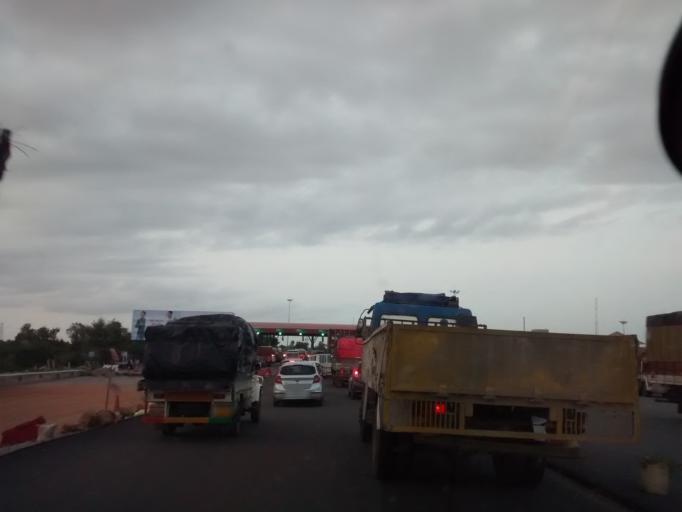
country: IN
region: Telangana
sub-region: Mahbubnagar
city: Farrukhnagar
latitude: 17.0049
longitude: 78.1944
